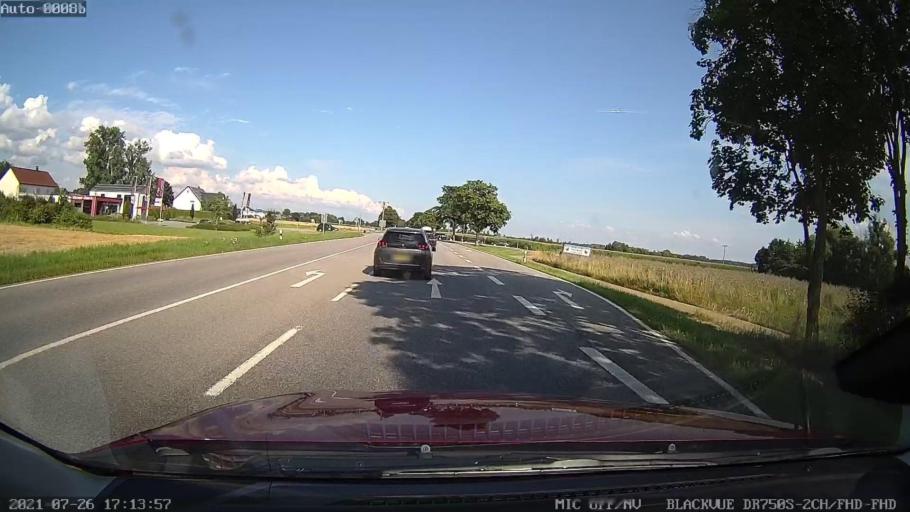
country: DE
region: Bavaria
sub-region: Upper Palatinate
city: Riekofen
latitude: 48.9679
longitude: 12.3248
